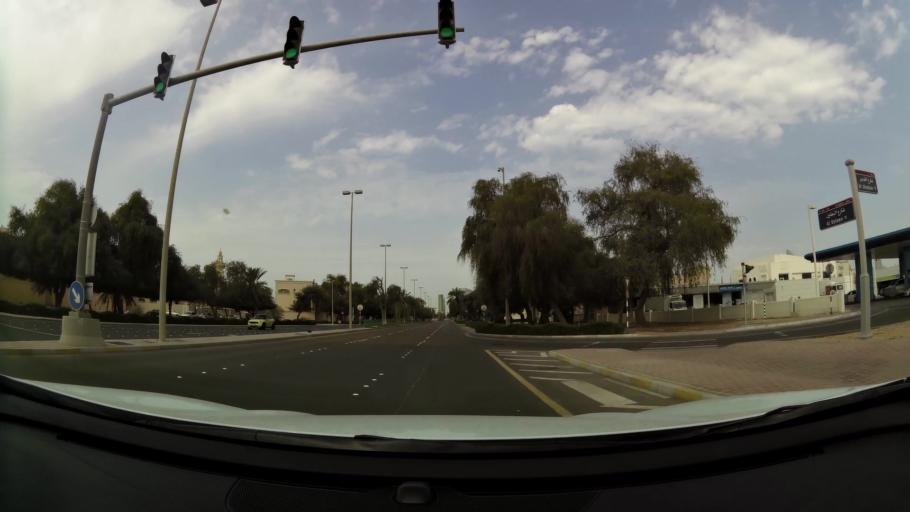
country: AE
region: Abu Dhabi
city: Abu Dhabi
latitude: 24.4576
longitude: 54.3489
